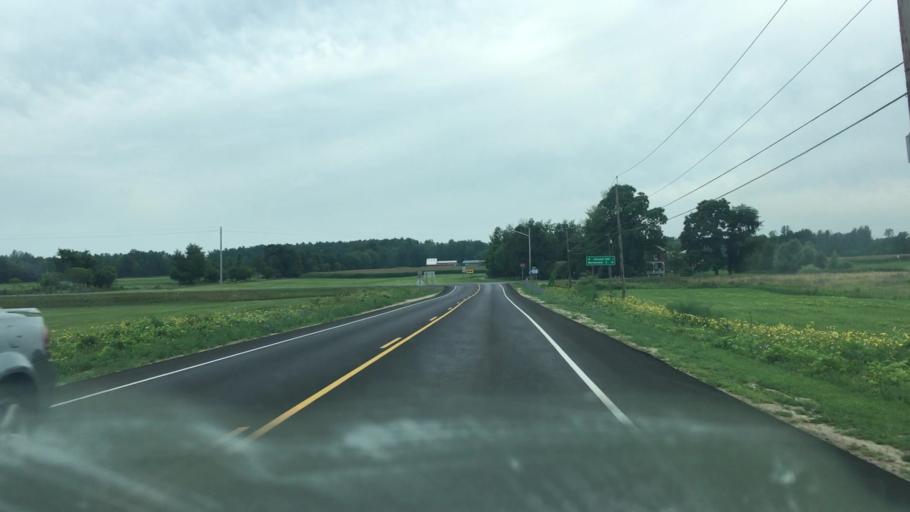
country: US
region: New York
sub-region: Clinton County
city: Morrisonville
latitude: 44.6485
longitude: -73.5668
